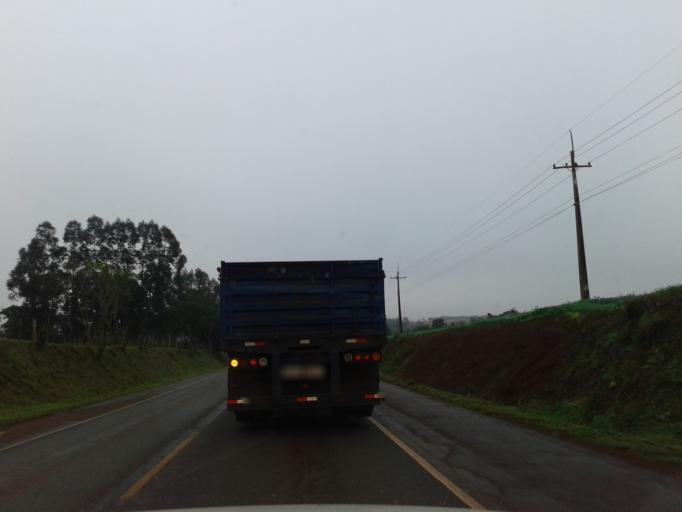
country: PY
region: Alto Parana
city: Naranjal
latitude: -25.9573
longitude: -55.1214
